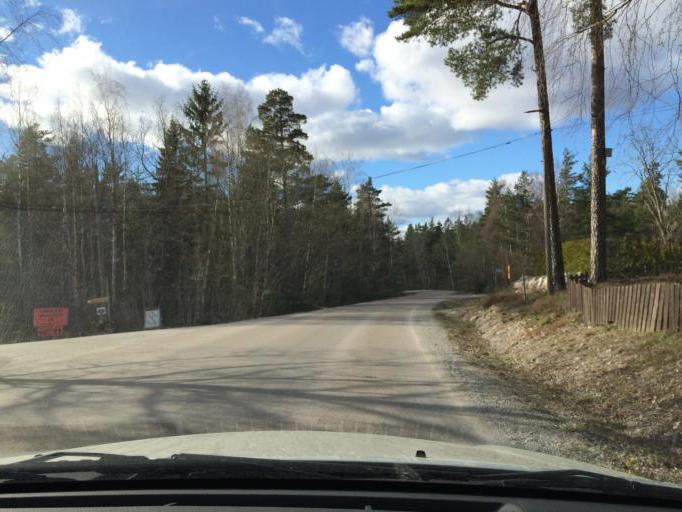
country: SE
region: Soedermanland
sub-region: Eskilstuna Kommun
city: Hallbybrunn
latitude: 59.4270
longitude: 16.4259
